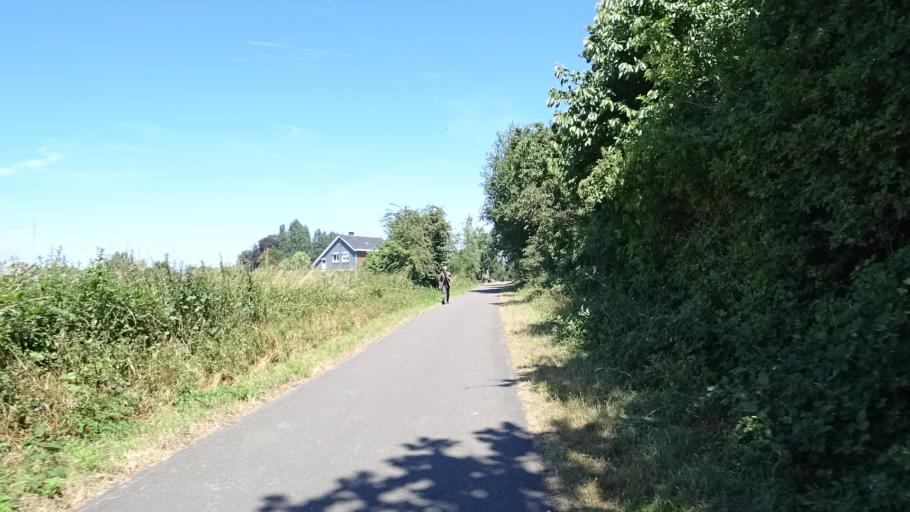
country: BE
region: Wallonia
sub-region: Province de Namur
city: Gembloux
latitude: 50.5847
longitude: 4.7162
